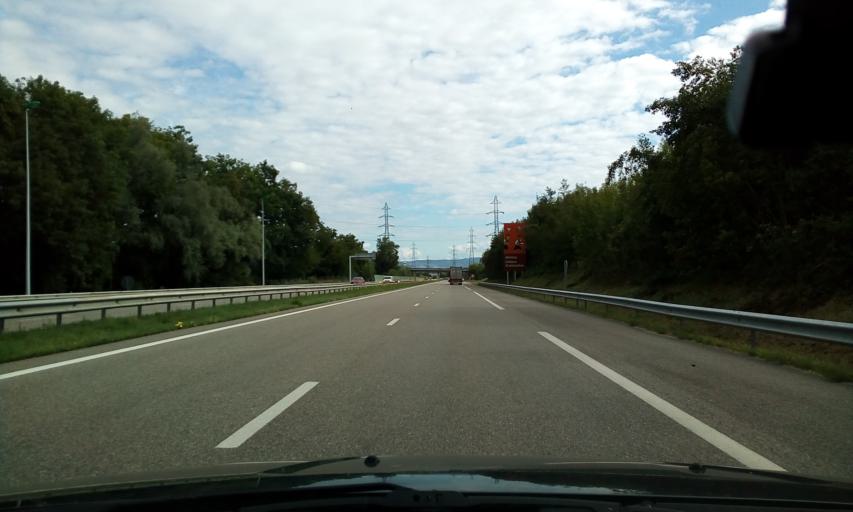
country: FR
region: Rhone-Alpes
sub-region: Departement de la Haute-Savoie
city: Seynod
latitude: 45.8776
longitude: 6.0728
